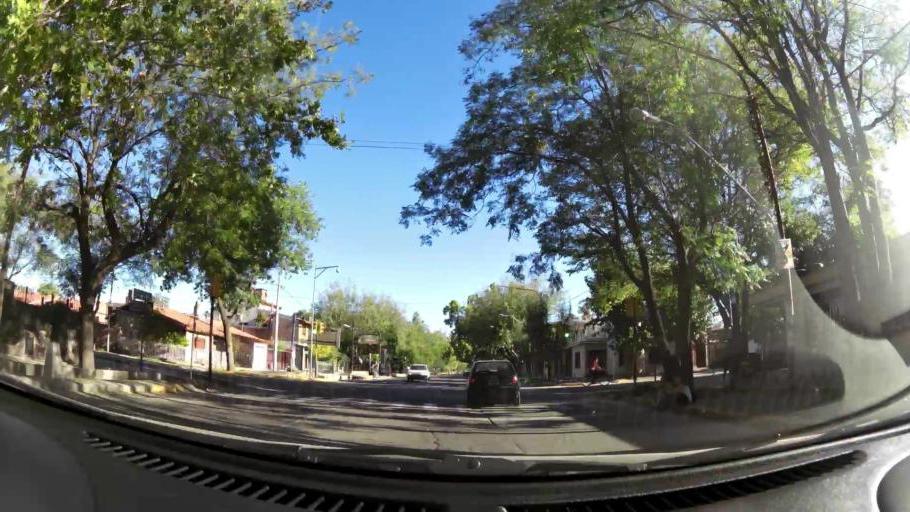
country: AR
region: Mendoza
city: Las Heras
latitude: -32.8570
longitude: -68.8272
